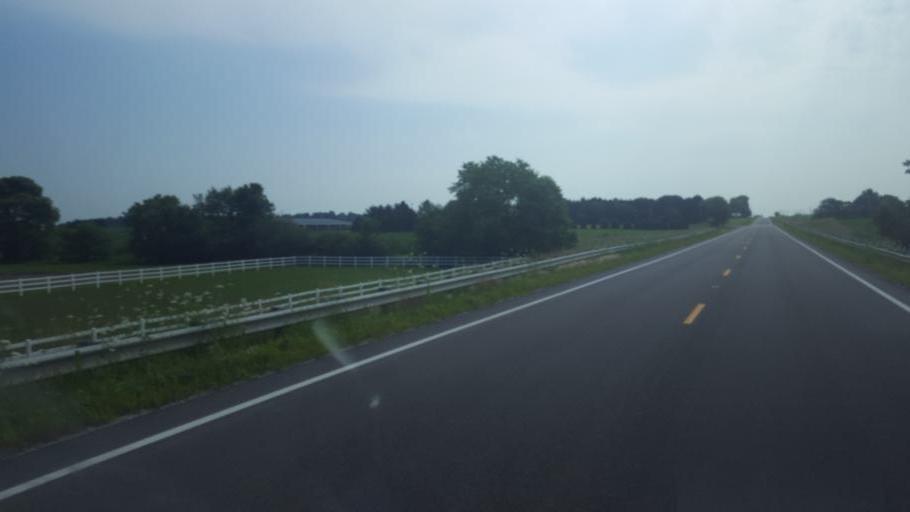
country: US
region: Ohio
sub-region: Hardin County
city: Kenton
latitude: 40.6441
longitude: -83.5582
